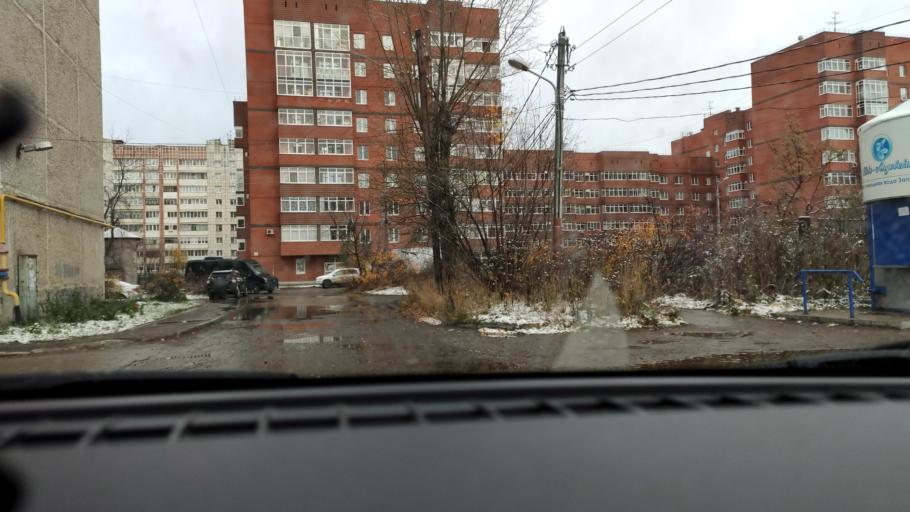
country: RU
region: Perm
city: Perm
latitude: 58.0293
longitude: 56.3261
